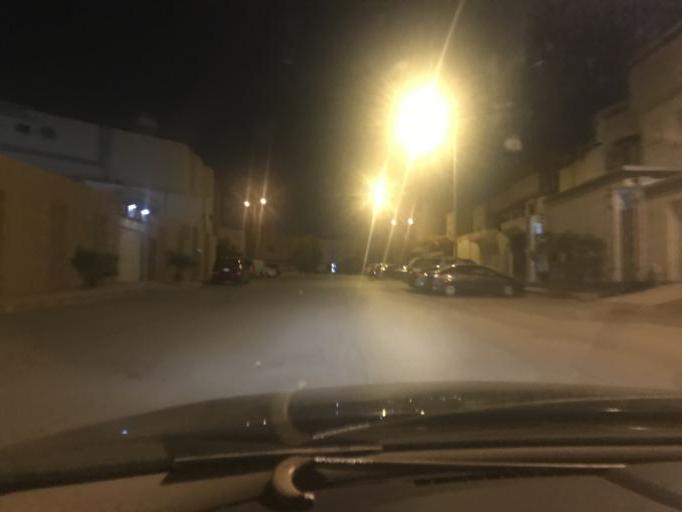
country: SA
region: Ar Riyad
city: Riyadh
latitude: 24.7583
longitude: 46.7617
